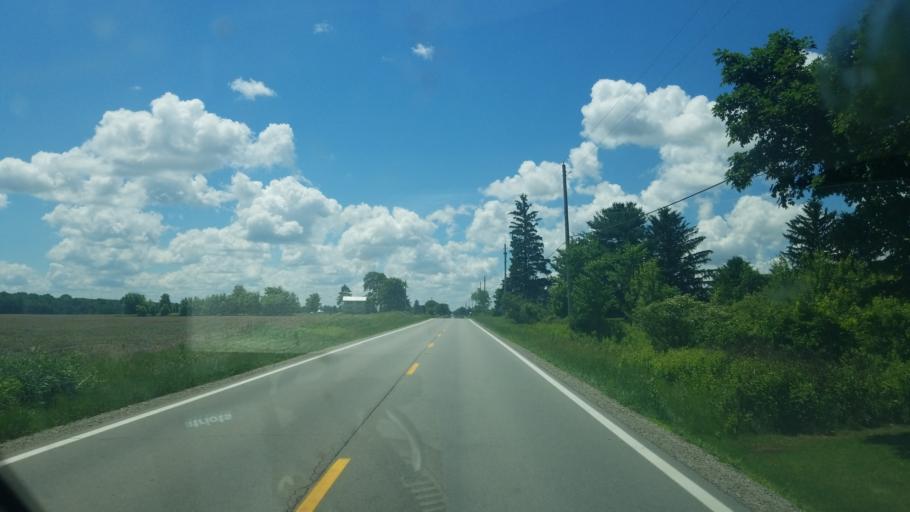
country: US
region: Ohio
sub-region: Huron County
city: New London
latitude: 41.1670
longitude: -82.4104
